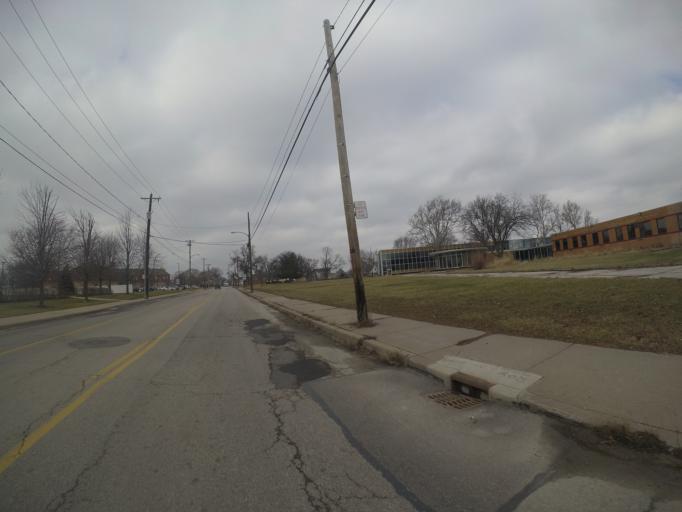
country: US
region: Ohio
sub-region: Lucas County
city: Oregon
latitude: 41.6199
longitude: -83.5139
